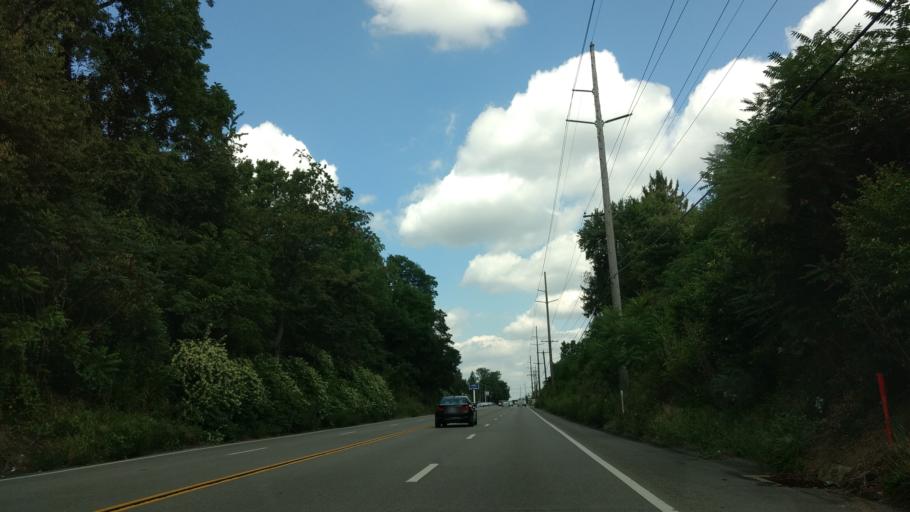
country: US
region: Pennsylvania
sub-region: Allegheny County
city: Franklin Park
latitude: 40.5763
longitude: -80.0373
